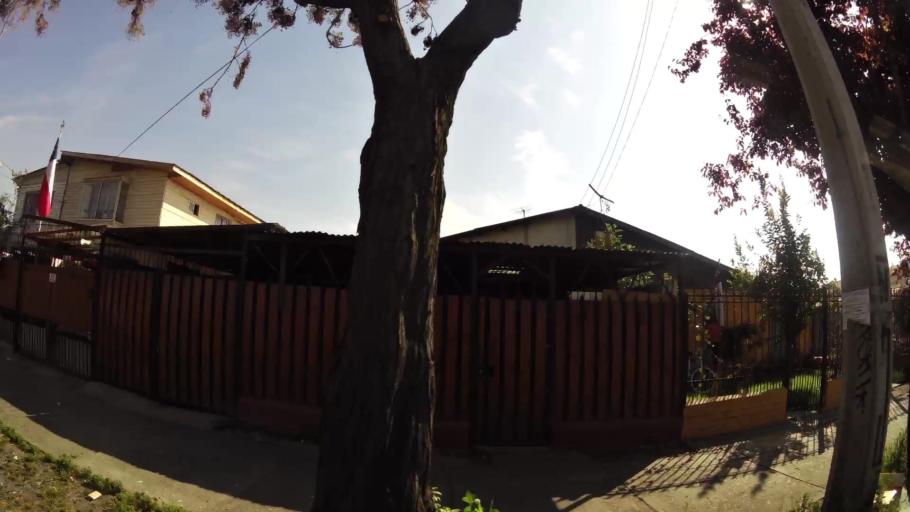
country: CL
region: Santiago Metropolitan
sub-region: Provincia de Santiago
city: La Pintana
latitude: -33.5626
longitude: -70.6545
